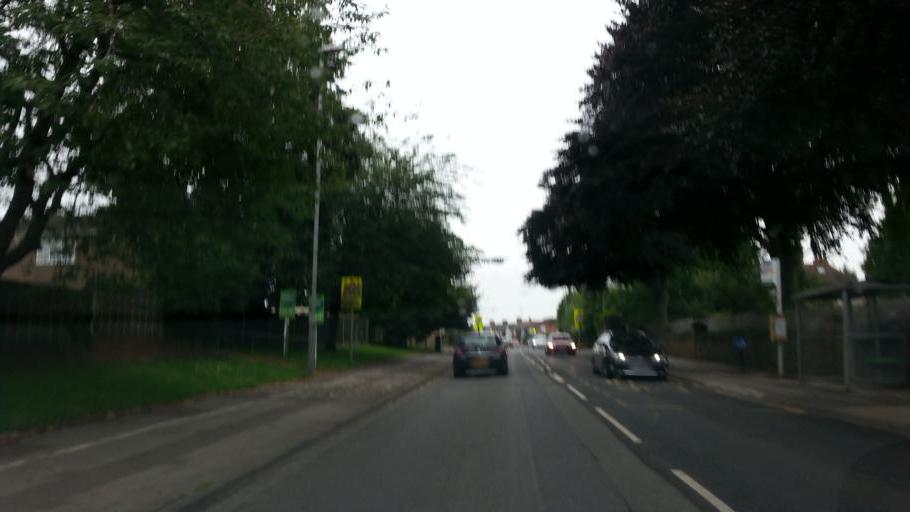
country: GB
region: England
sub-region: Nottinghamshire
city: Hucknall
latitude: 53.0313
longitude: -1.2108
